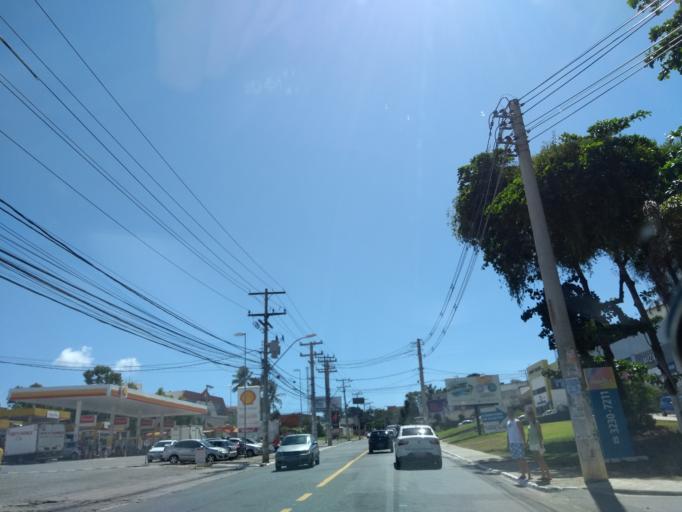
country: BR
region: Bahia
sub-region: Salvador
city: Salvador
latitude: -12.9690
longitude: -38.4252
